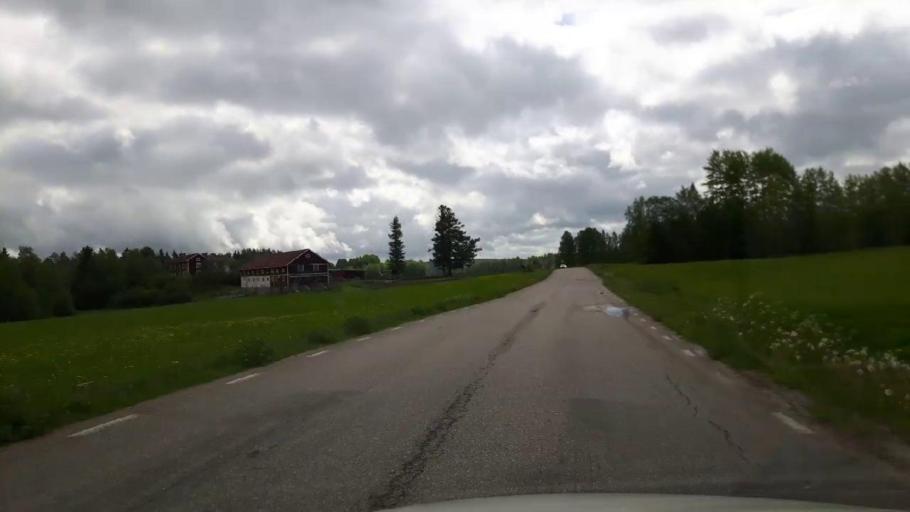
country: SE
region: Gaevleborg
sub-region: Ovanakers Kommun
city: Edsbyn
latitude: 61.3541
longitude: 15.9130
